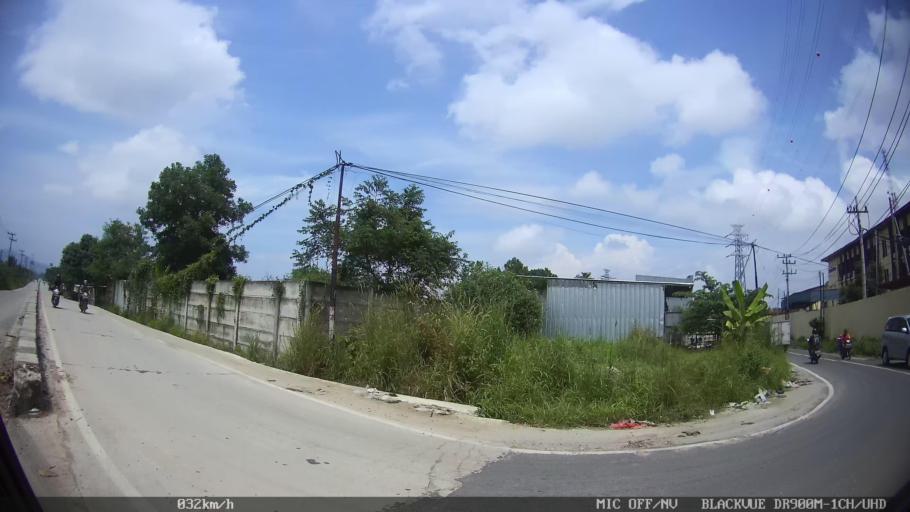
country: ID
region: Lampung
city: Kedaton
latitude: -5.3614
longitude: 105.3083
